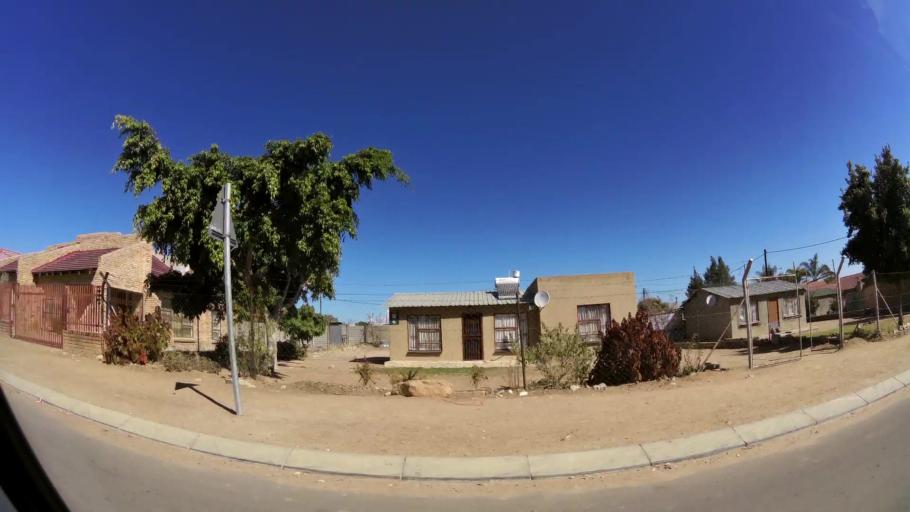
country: ZA
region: Limpopo
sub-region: Capricorn District Municipality
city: Polokwane
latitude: -23.8548
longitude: 29.4103
